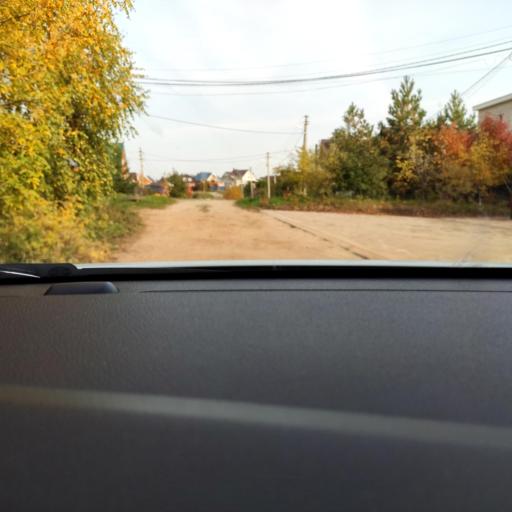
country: RU
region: Tatarstan
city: Vysokaya Gora
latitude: 55.8108
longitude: 49.2457
